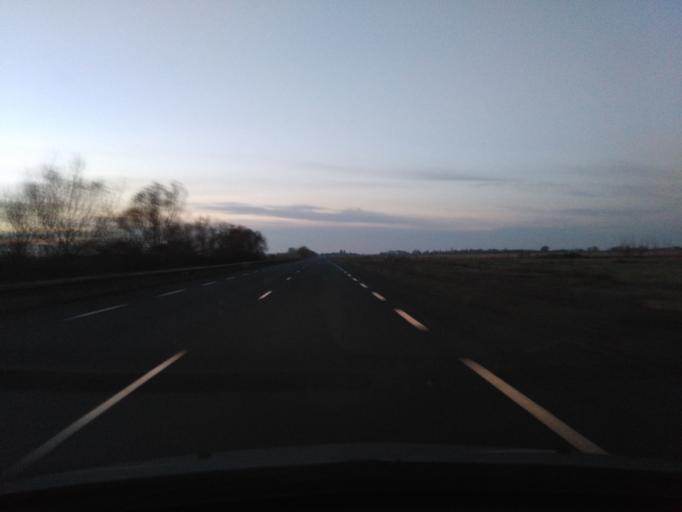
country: FR
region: Pays de la Loire
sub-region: Departement de la Vendee
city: Champagne-les-Marais
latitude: 46.3903
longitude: -1.0939
